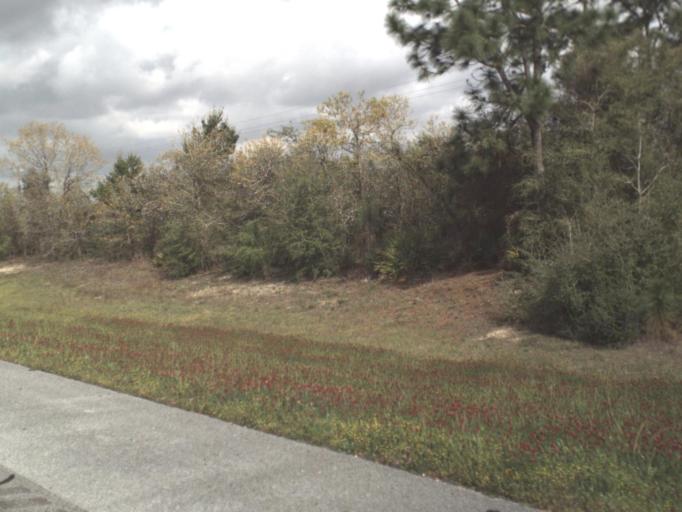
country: US
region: Florida
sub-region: Okaloosa County
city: Crestview
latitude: 30.7208
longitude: -86.4737
